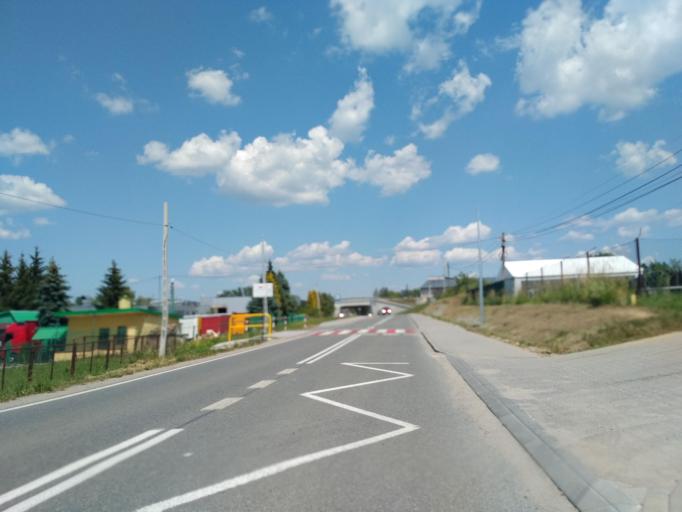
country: PL
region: Subcarpathian Voivodeship
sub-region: Powiat sanocki
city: Sanok
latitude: 49.5621
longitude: 22.1535
